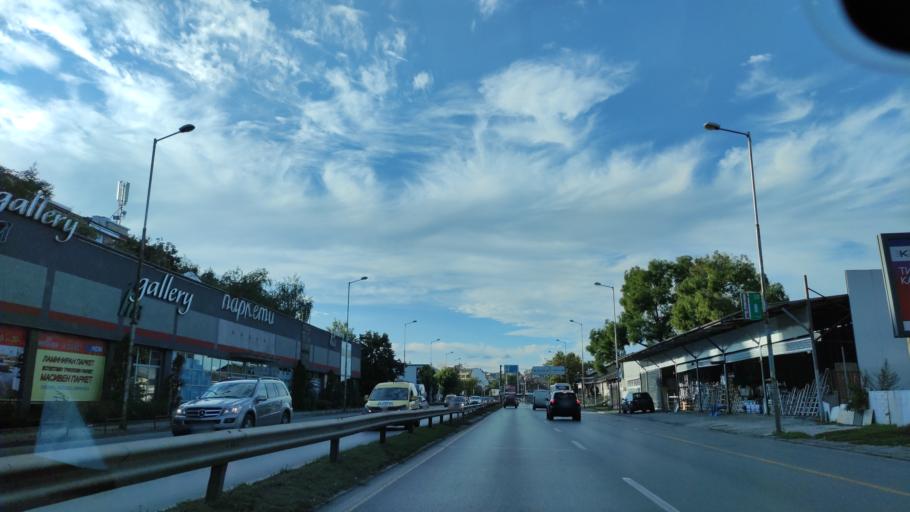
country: BG
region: Sofia-Capital
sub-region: Stolichna Obshtina
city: Sofia
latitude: 42.7035
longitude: 23.3362
